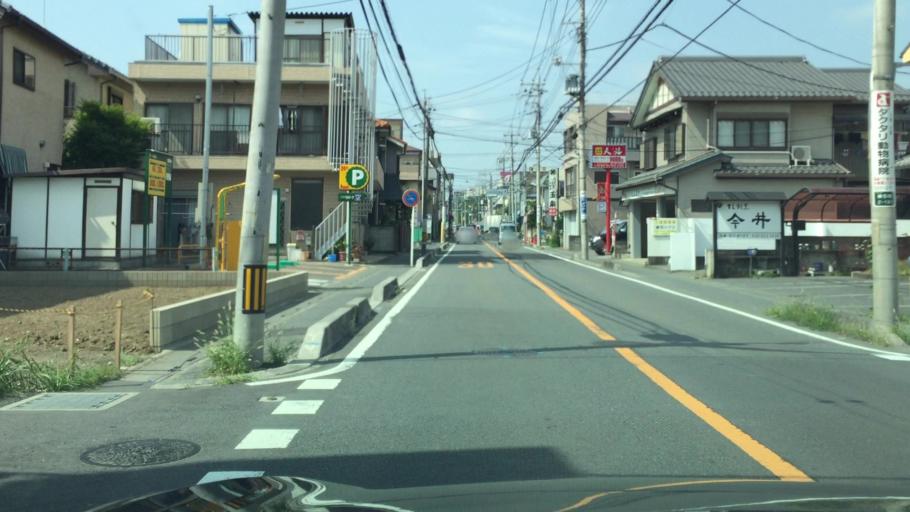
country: JP
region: Saitama
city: Yono
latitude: 35.9173
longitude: 139.6085
